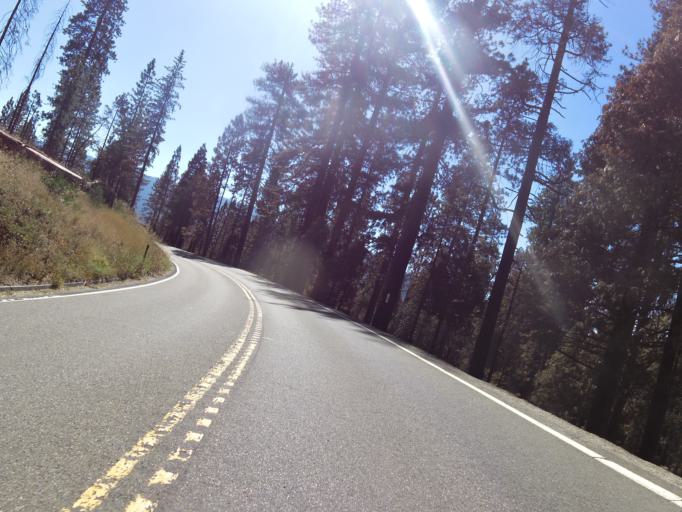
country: US
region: California
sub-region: Mariposa County
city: Yosemite Valley
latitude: 37.5905
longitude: -119.6888
